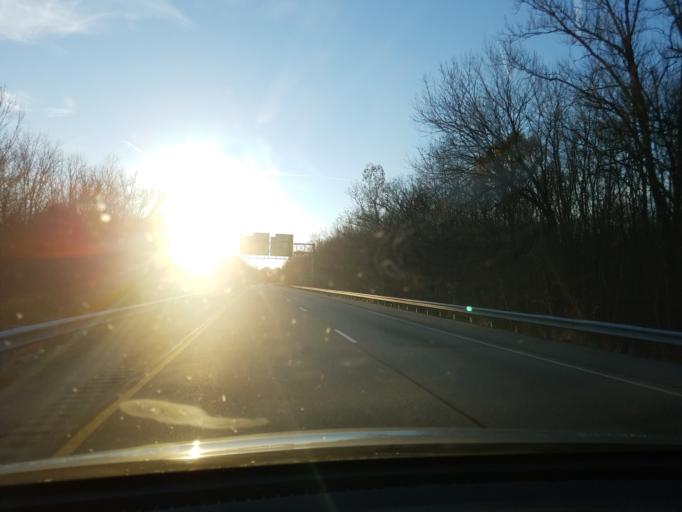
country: US
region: Indiana
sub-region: Warrick County
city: Chandler
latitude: 38.1727
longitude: -87.4241
